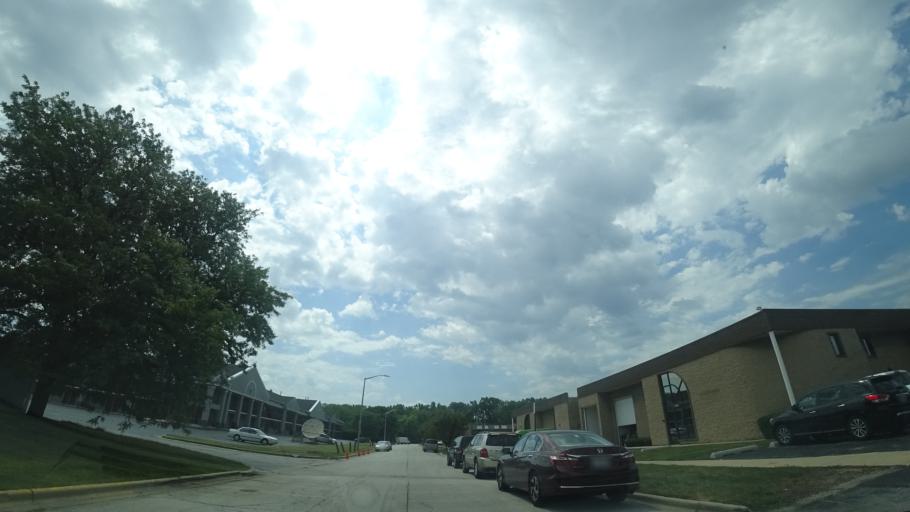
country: US
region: Illinois
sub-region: Cook County
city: Crestwood
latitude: 41.6633
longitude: -87.7461
